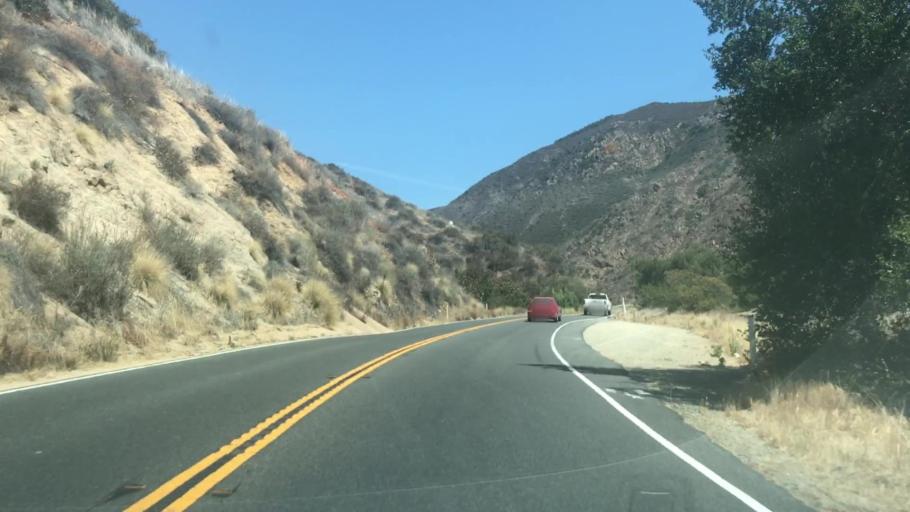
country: US
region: California
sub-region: Orange County
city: Coto De Caza
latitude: 33.5924
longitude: -117.5108
